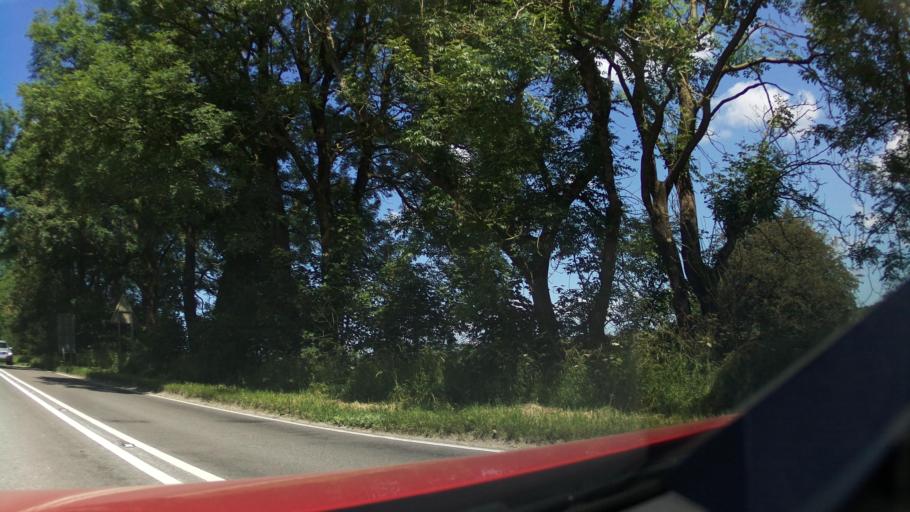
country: GB
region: England
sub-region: Derbyshire
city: Buxton
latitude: 53.2266
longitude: -1.8740
